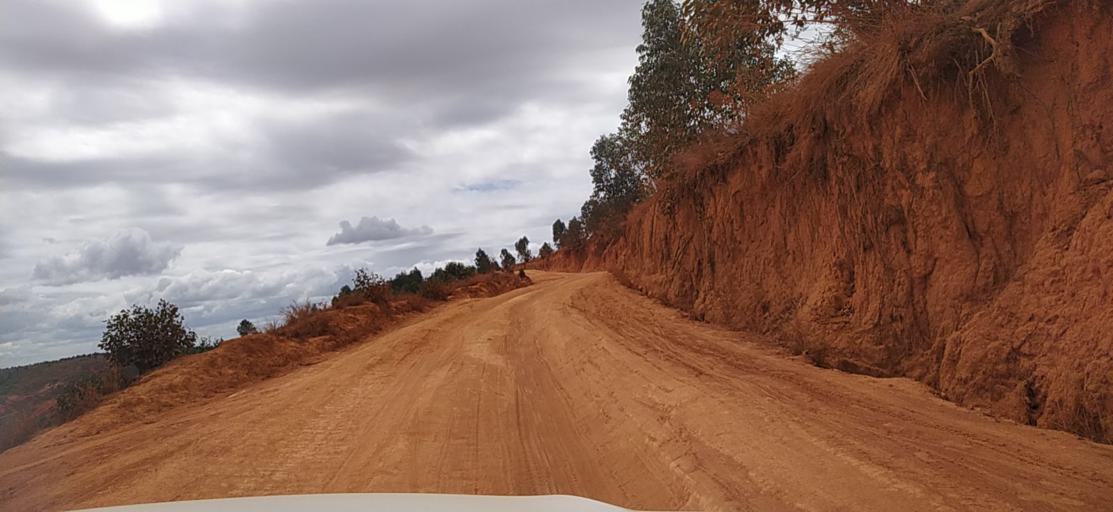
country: MG
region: Alaotra Mangoro
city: Ambatondrazaka
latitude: -18.0491
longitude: 48.2495
